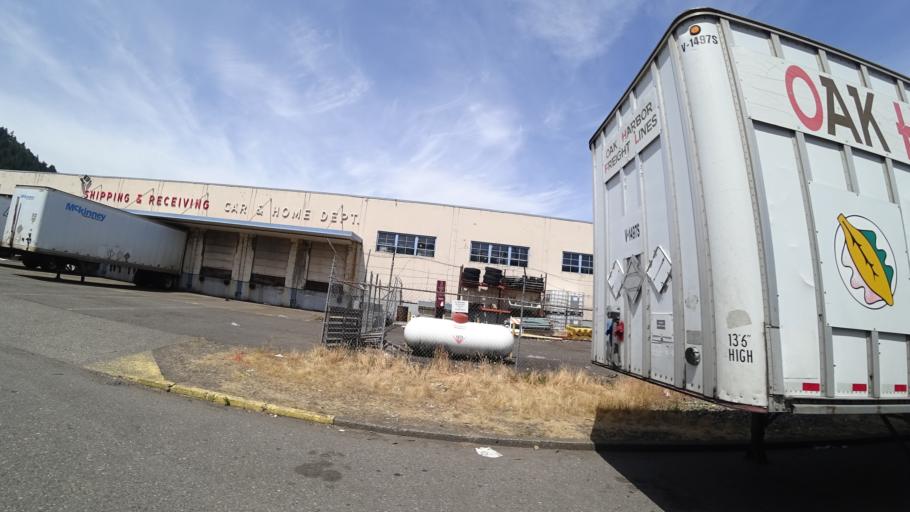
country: US
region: Oregon
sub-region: Multnomah County
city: Portland
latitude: 45.5412
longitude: -122.7174
